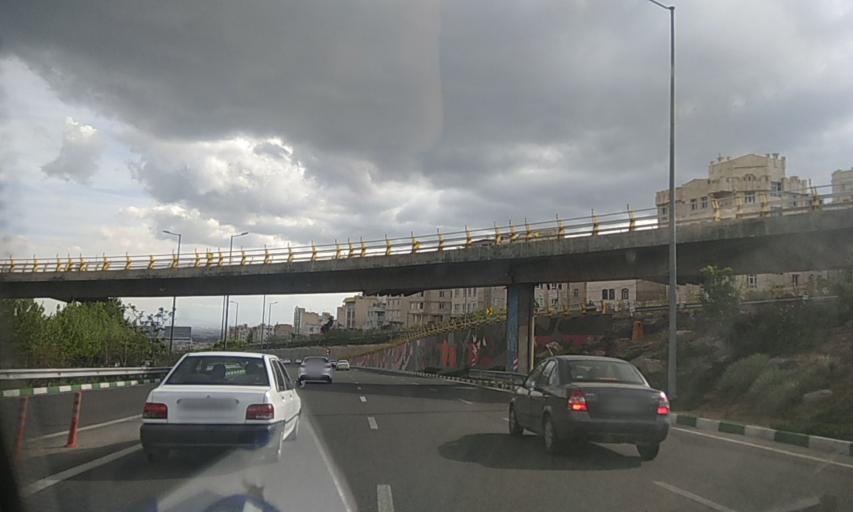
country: IR
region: Tehran
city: Tajrish
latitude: 35.7629
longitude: 51.2963
